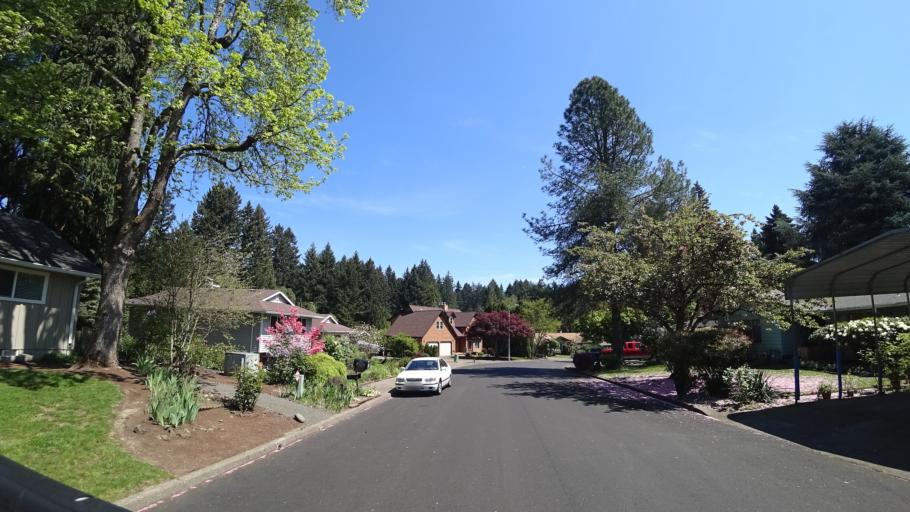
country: US
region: Oregon
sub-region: Washington County
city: Hillsboro
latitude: 45.5167
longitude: -122.9613
